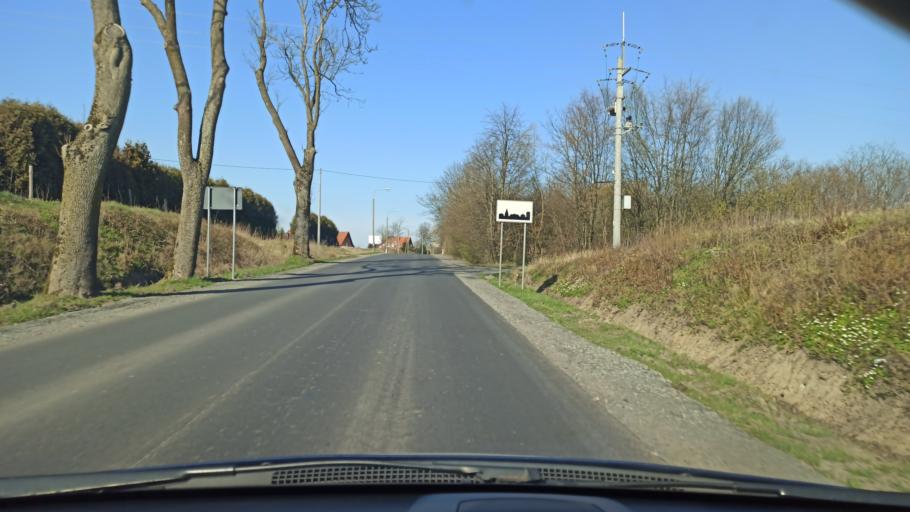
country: PL
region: Warmian-Masurian Voivodeship
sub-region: Powiat elblaski
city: Gronowo Gorne
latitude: 54.2072
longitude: 19.5041
